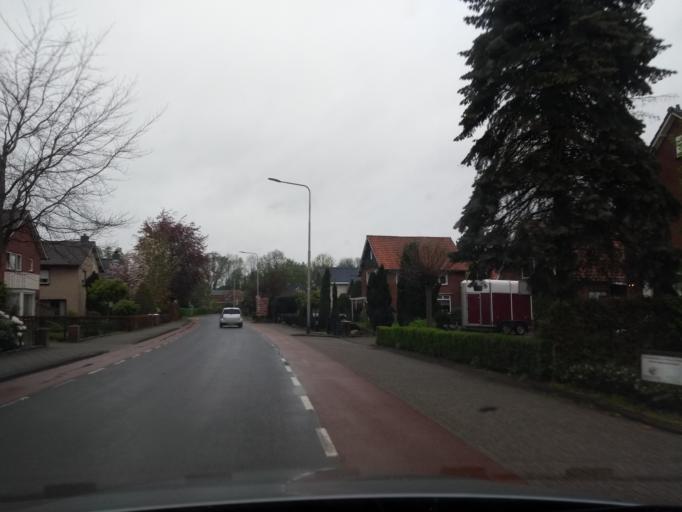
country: DE
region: Lower Saxony
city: Getelo
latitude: 52.4122
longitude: 6.9017
